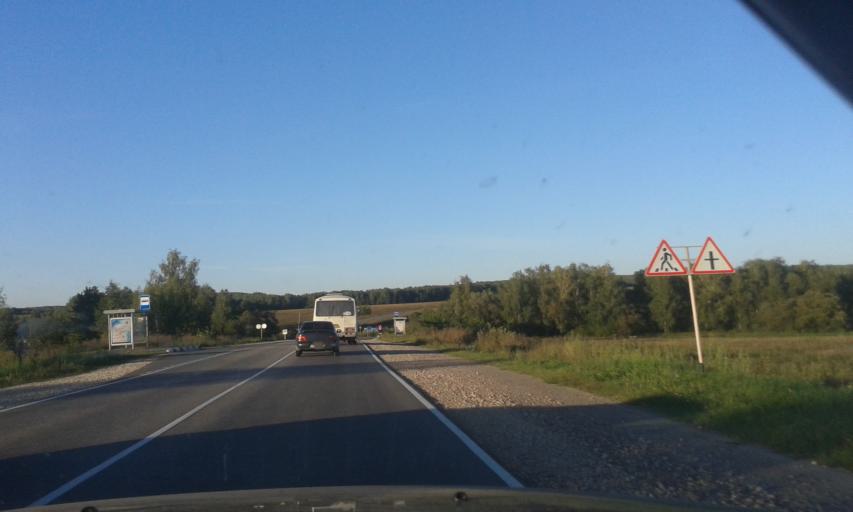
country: RU
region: Tula
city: Krapivna
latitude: 54.1155
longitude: 37.2213
